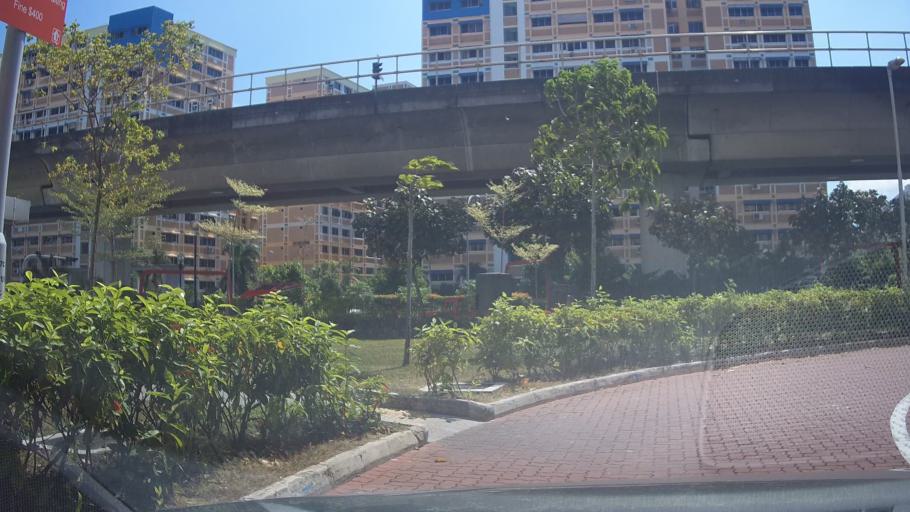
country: MY
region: Johor
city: Kampung Pasir Gudang Baru
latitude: 1.3691
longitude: 103.9476
